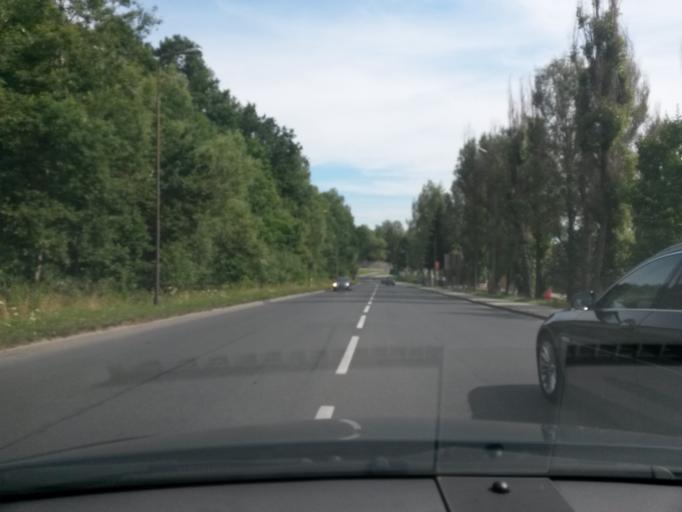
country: PL
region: Lower Silesian Voivodeship
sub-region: Jelenia Gora
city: Jelenia Gora
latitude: 50.9020
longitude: 15.7173
